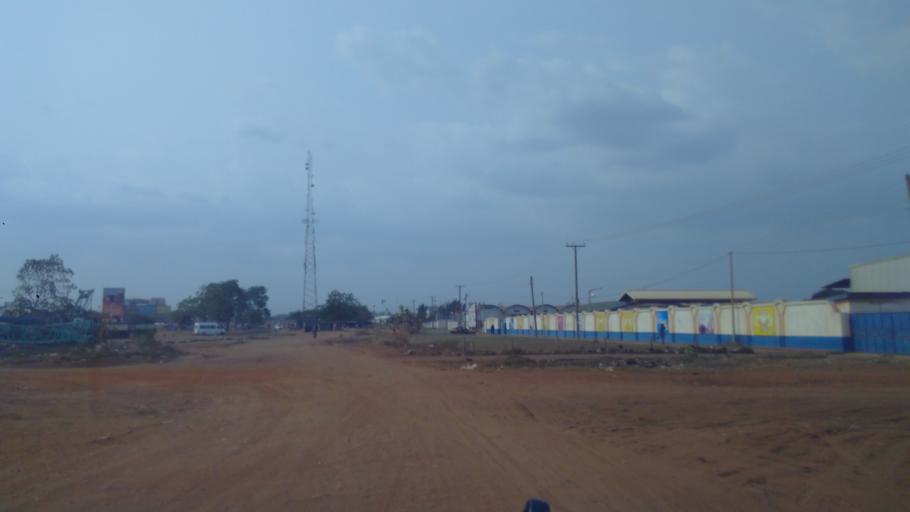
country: GH
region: Greater Accra
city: Tema
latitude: 5.6806
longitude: -0.0118
